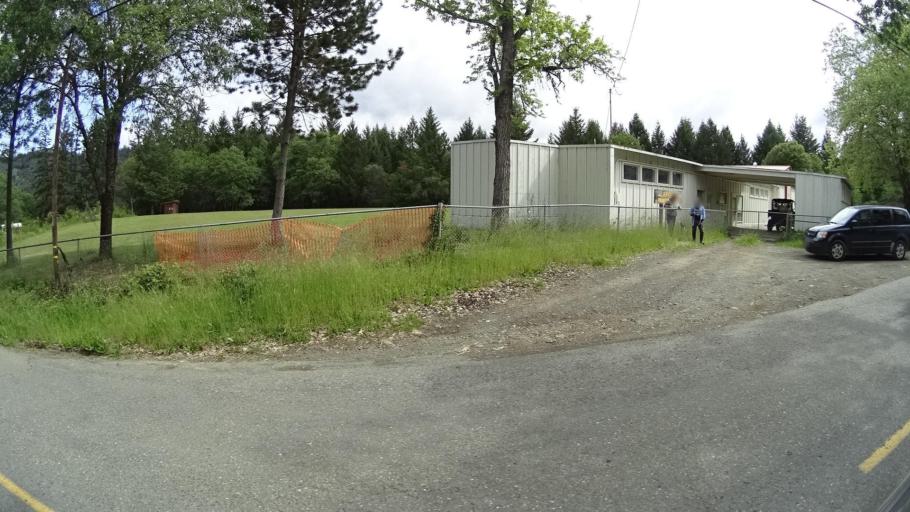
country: US
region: California
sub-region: Humboldt County
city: Redway
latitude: 40.1733
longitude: -123.6102
